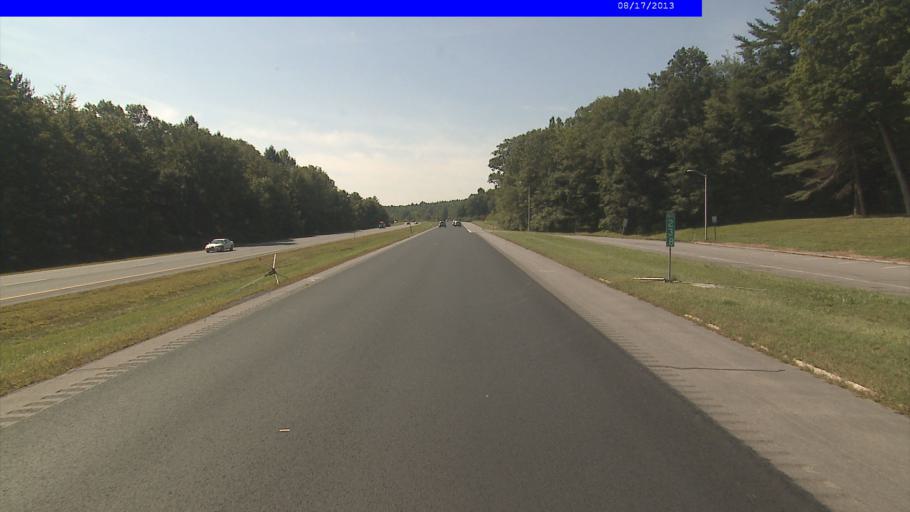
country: US
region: New Hampshire
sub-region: Cheshire County
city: Westmoreland
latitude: 43.0242
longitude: -72.4721
